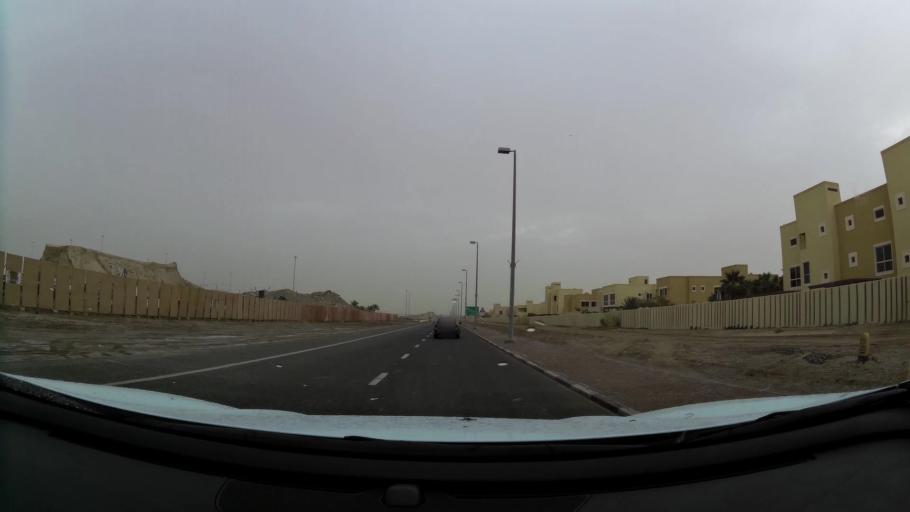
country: AE
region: Abu Dhabi
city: Abu Dhabi
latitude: 24.4402
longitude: 54.5910
